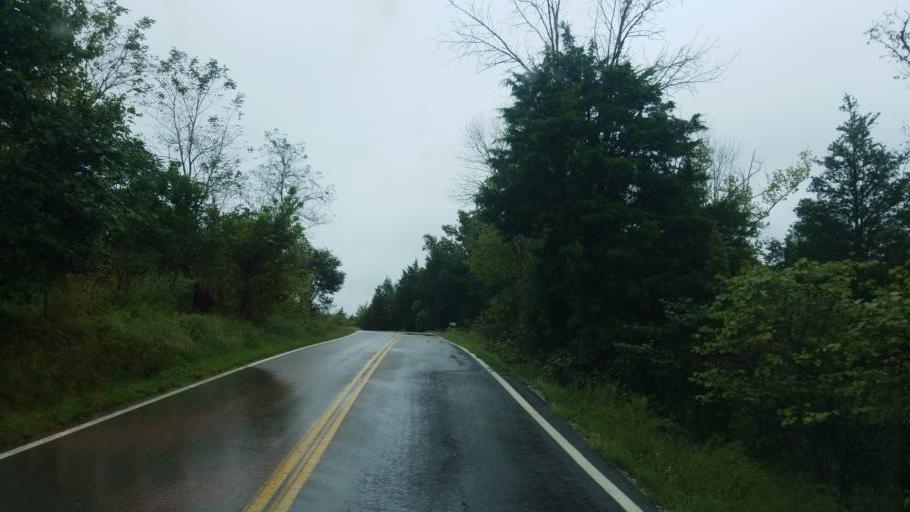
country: US
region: Ohio
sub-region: Adams County
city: West Union
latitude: 38.7727
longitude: -83.5322
